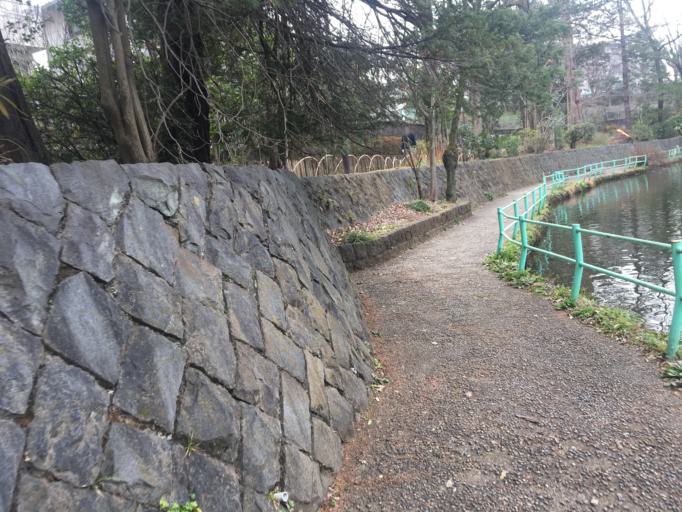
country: JP
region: Tokyo
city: Musashino
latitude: 35.7257
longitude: 139.5668
